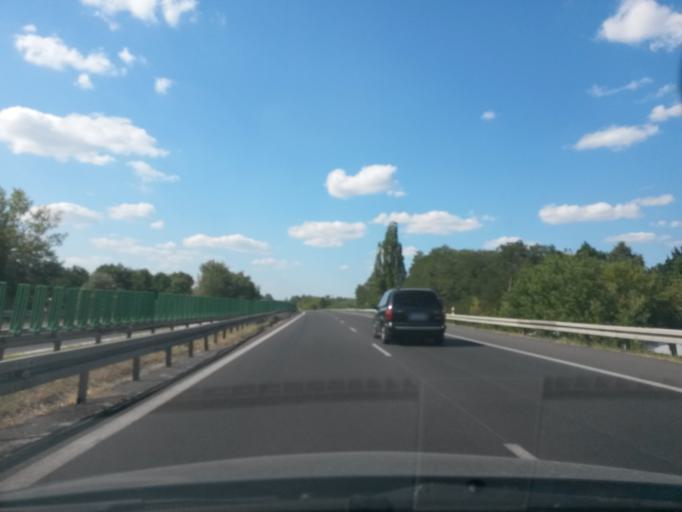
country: PL
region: Masovian Voivodeship
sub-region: Powiat nowodworski
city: Nowy Dwor Mazowiecki
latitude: 52.3934
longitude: 20.7208
